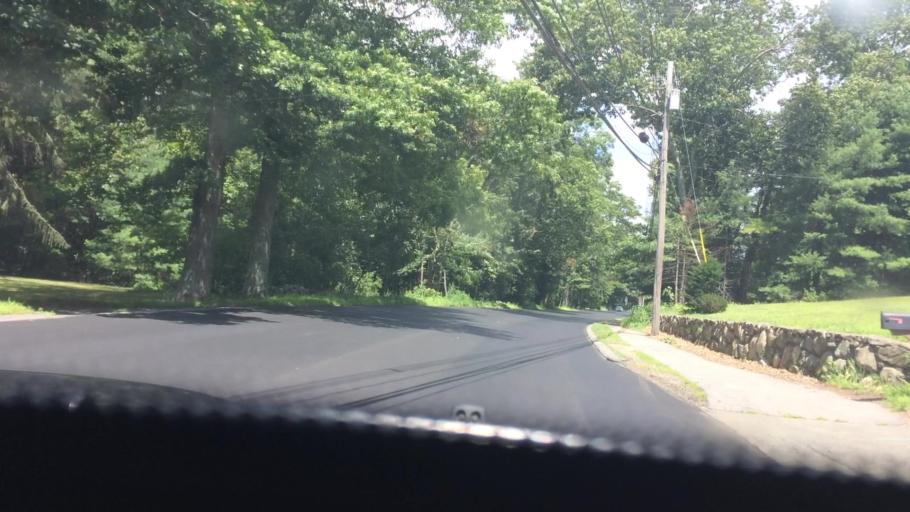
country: US
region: Massachusetts
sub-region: Middlesex County
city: Sudbury
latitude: 42.4020
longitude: -71.4359
